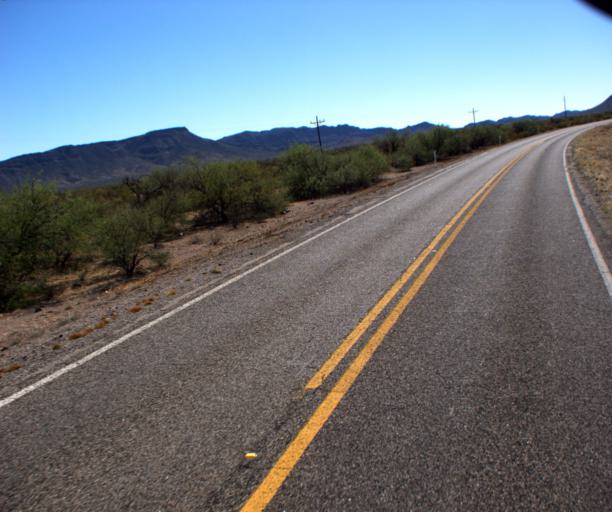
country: US
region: Arizona
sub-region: Pima County
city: Ajo
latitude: 32.3237
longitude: -112.7726
